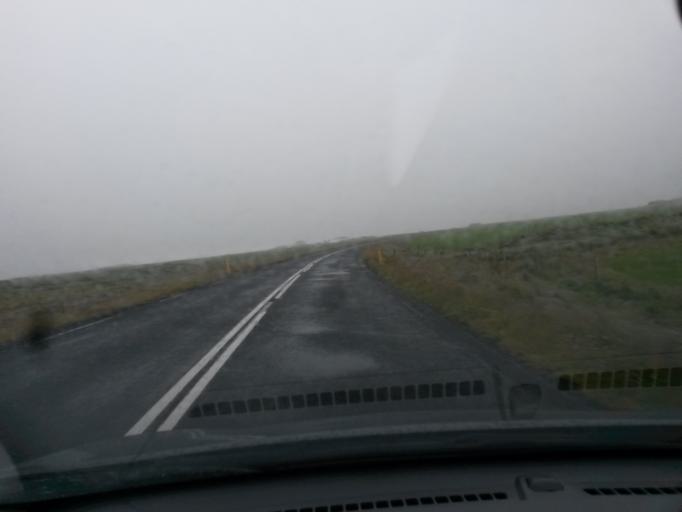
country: IS
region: South
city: Vestmannaeyjar
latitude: 63.4315
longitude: -19.1815
